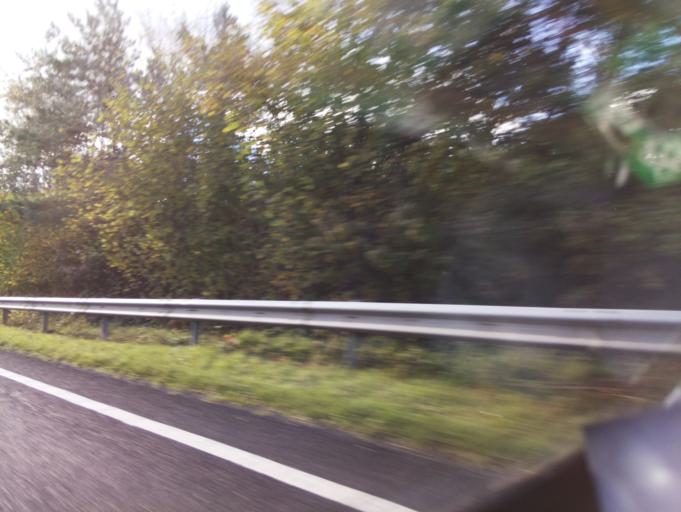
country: GB
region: Wales
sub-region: Sir Powys
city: Brecon
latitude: 51.9887
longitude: -3.3254
